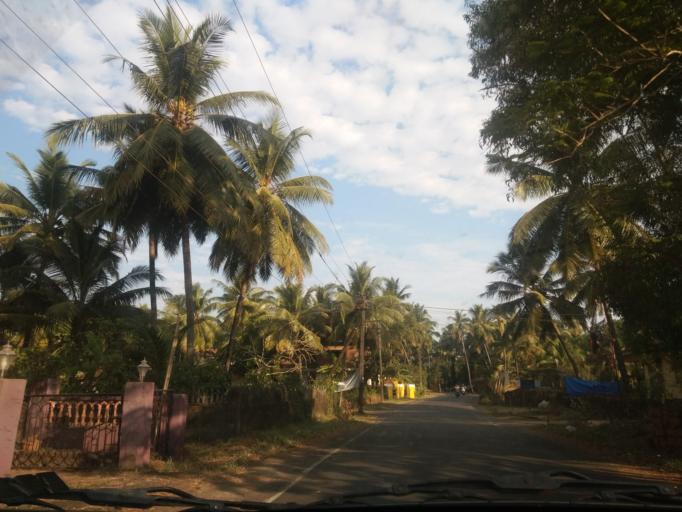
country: IN
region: Goa
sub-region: South Goa
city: Varca
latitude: 15.2501
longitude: 73.9563
